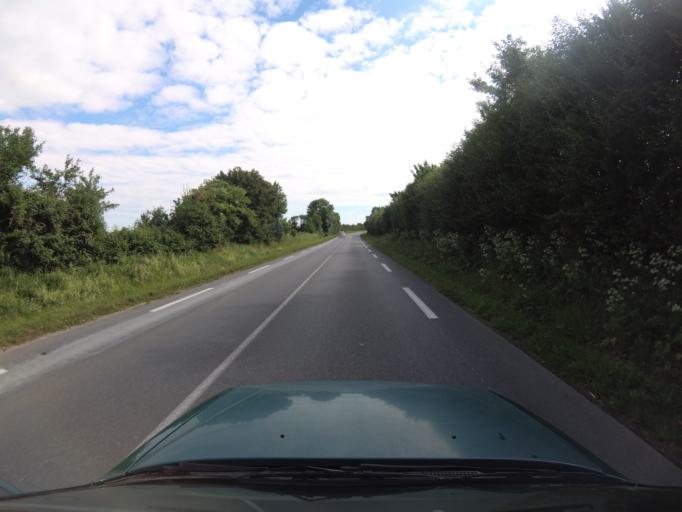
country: FR
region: Poitou-Charentes
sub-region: Departement de la Charente-Maritime
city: Saint-Xandre
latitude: 46.2215
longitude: -1.0858
